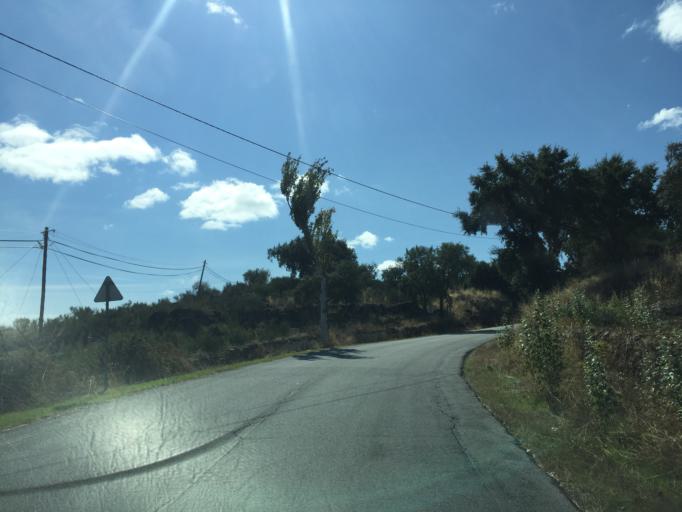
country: PT
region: Portalegre
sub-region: Marvao
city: Marvao
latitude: 39.4423
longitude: -7.3675
